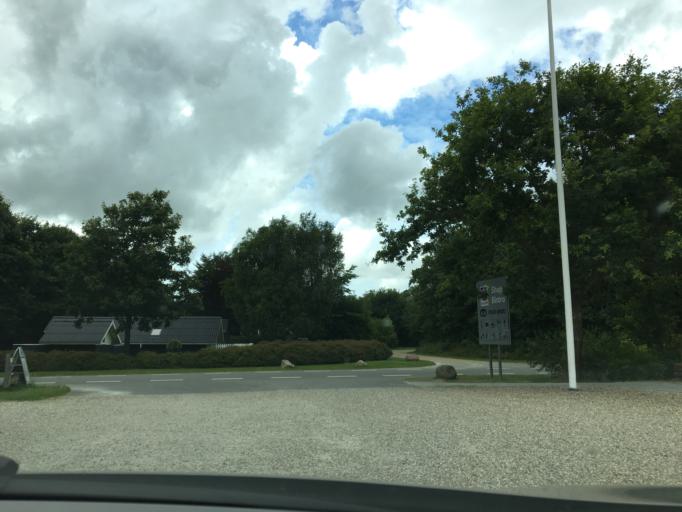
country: DK
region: South Denmark
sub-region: Varde Kommune
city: Oksbol
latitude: 55.6673
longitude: 8.3164
